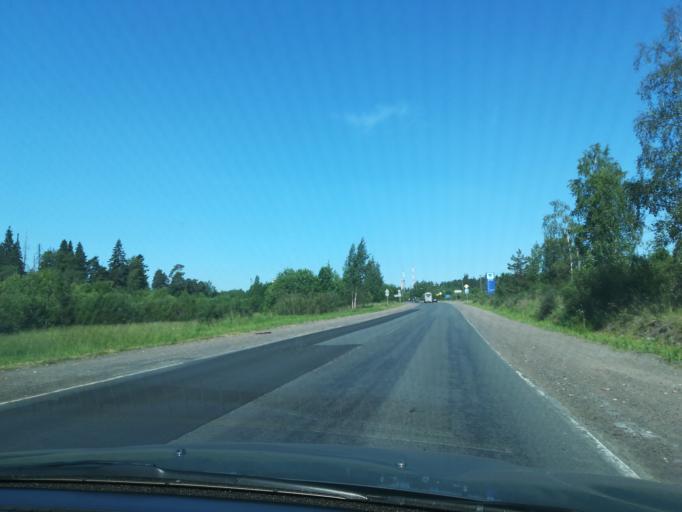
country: RU
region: Leningrad
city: Svetogorsk
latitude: 61.0926
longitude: 28.8931
